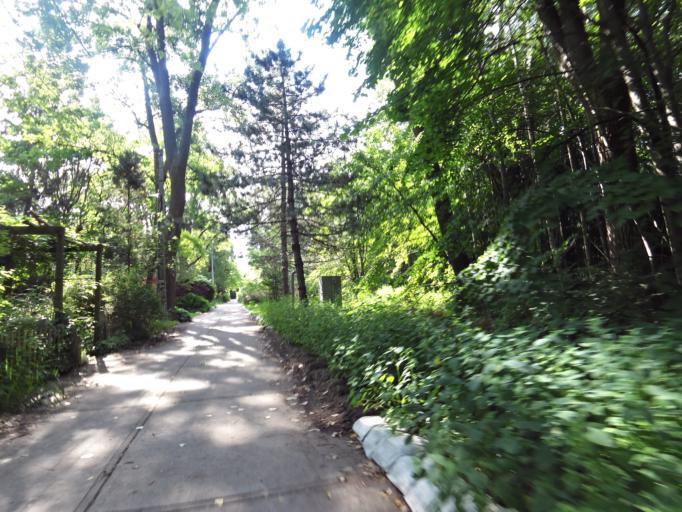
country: CA
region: Ontario
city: Toronto
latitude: 43.6270
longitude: -79.3614
